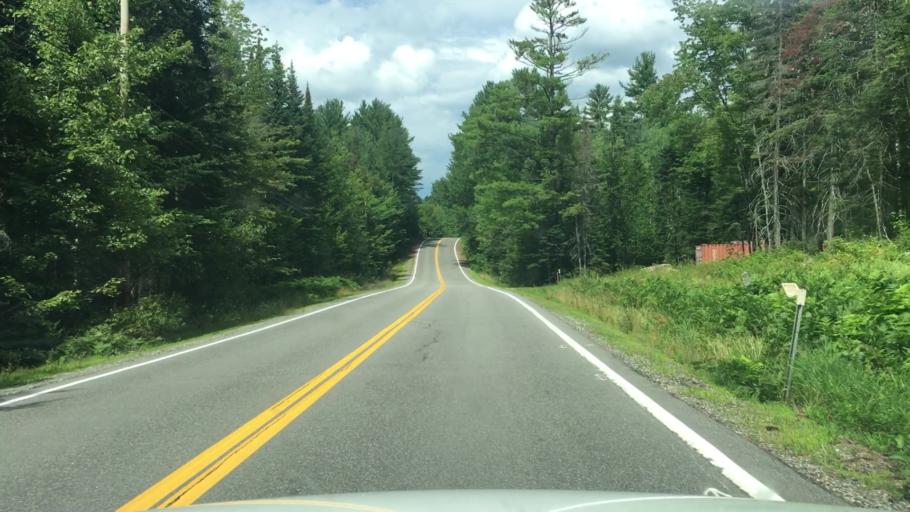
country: US
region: New Hampshire
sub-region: Grafton County
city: Deerfield
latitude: 44.3015
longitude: -71.6592
